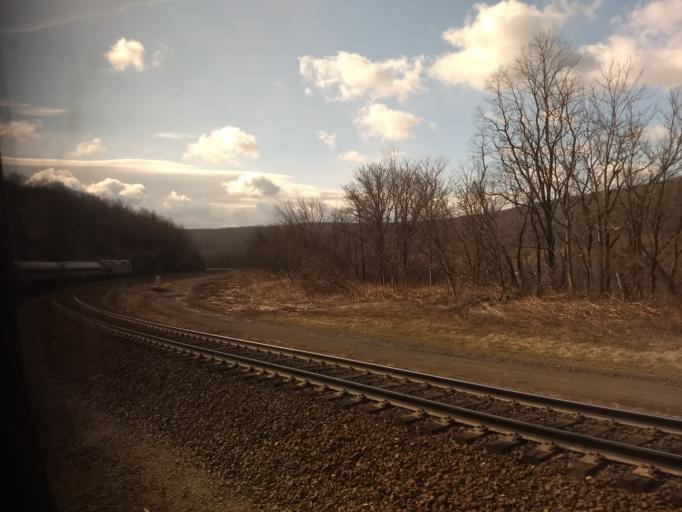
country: US
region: Pennsylvania
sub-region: Cambria County
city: Gallitzin
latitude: 40.4817
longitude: -78.5159
